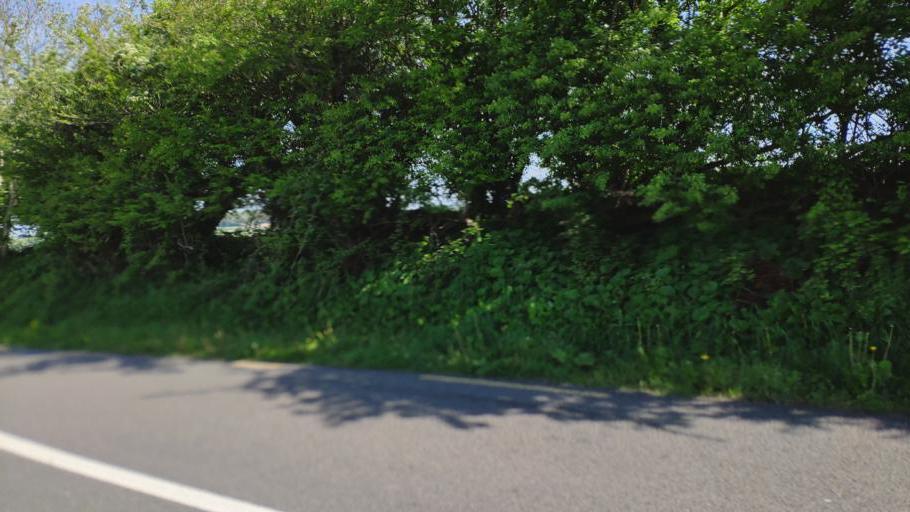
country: IE
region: Munster
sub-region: County Cork
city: Blarney
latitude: 51.9233
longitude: -8.5536
